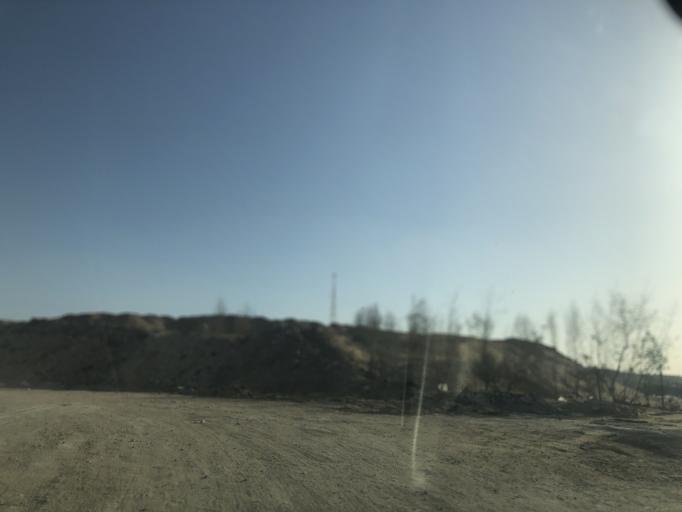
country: EG
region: Al Jizah
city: Al Jizah
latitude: 29.9915
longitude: 31.1105
